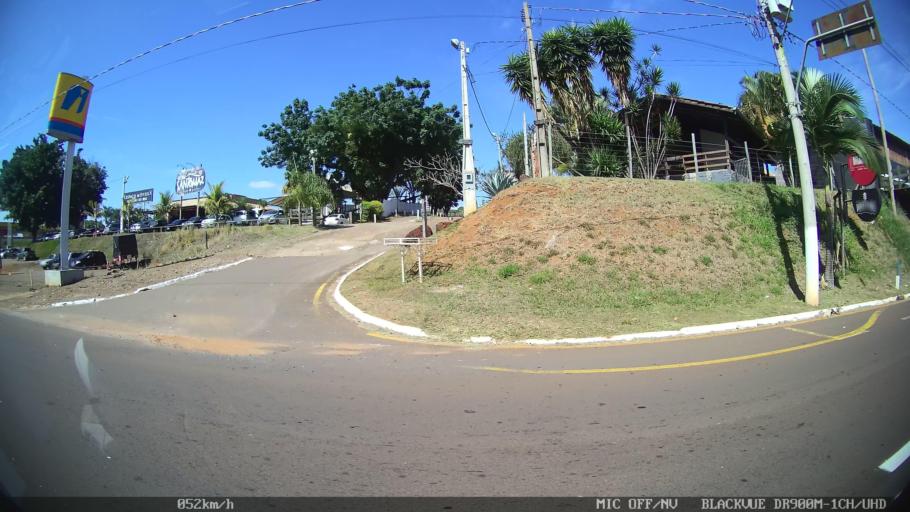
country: BR
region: Sao Paulo
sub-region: Franca
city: Franca
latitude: -20.5544
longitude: -47.4115
